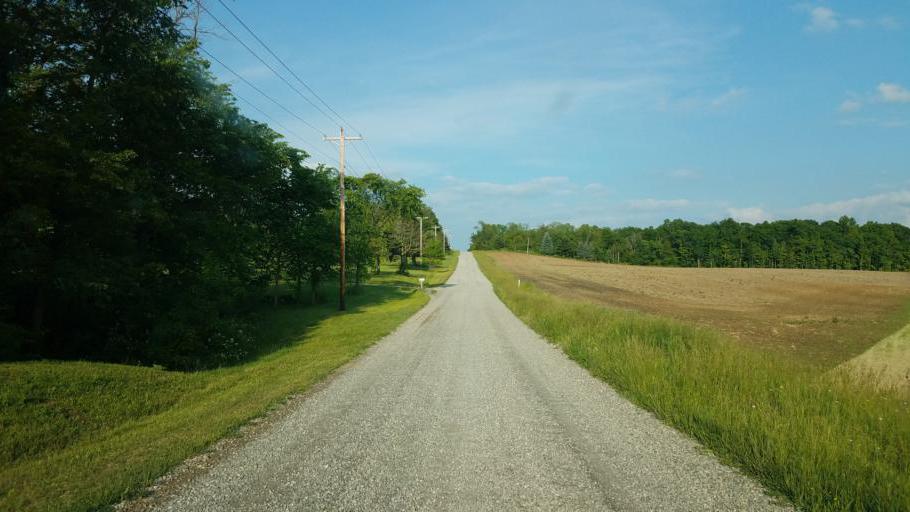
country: US
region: Ohio
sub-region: Morrow County
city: Cardington
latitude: 40.4243
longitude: -82.7994
